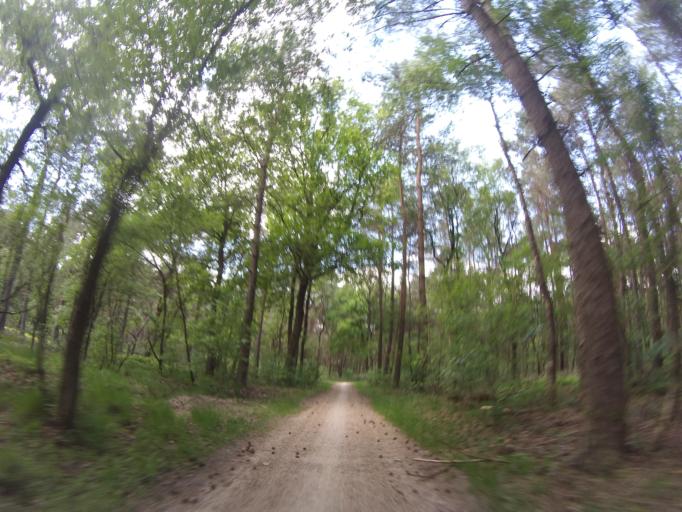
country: NL
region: Gelderland
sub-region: Gemeente Barneveld
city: Stroe
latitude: 52.1709
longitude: 5.7156
